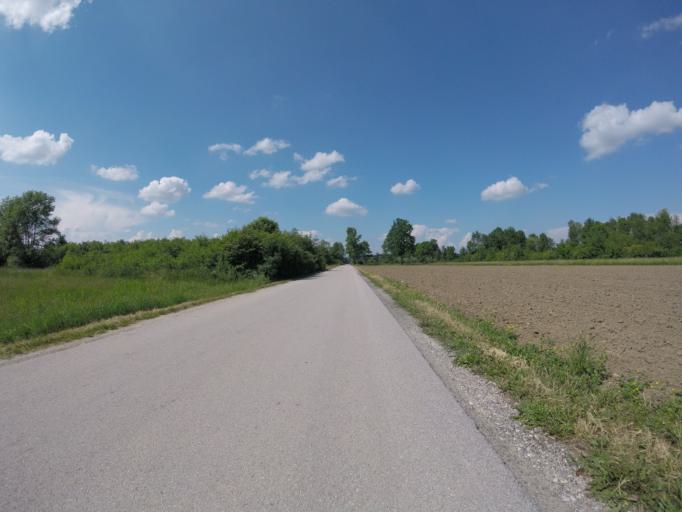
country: HR
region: Zagrebacka
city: Kuce
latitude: 45.6717
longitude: 16.1838
